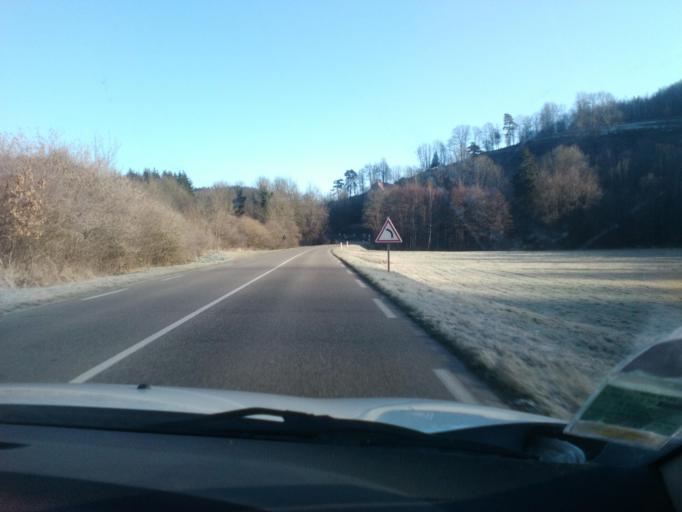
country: FR
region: Alsace
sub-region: Departement du Bas-Rhin
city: Rothau
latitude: 48.4467
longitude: 7.1957
